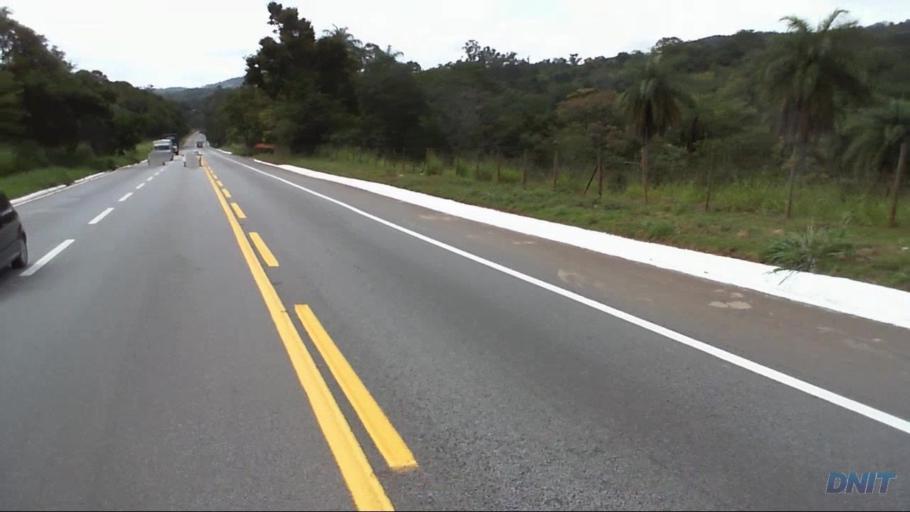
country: BR
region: Minas Gerais
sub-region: Santa Luzia
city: Santa Luzia
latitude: -19.7990
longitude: -43.7490
